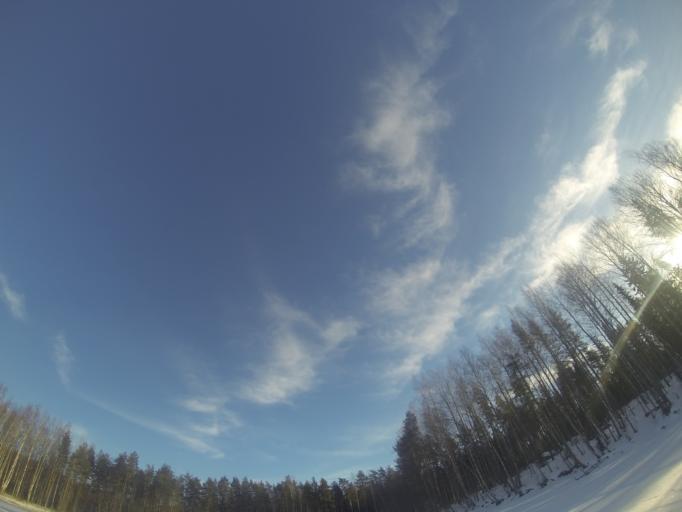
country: FI
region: Southern Savonia
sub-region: Savonlinna
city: Savonlinna
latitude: 61.8793
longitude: 28.9216
